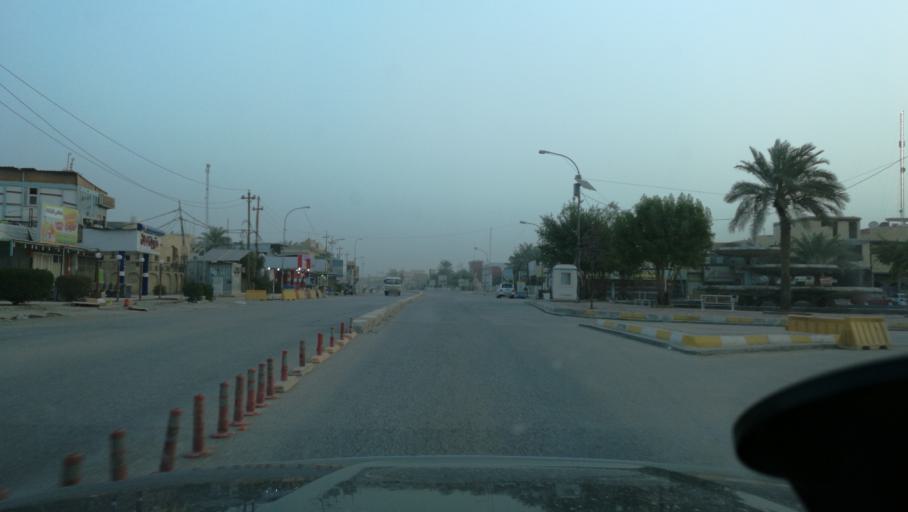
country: IQ
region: Dhi Qar
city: An Nasiriyah
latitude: 31.0460
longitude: 46.2450
